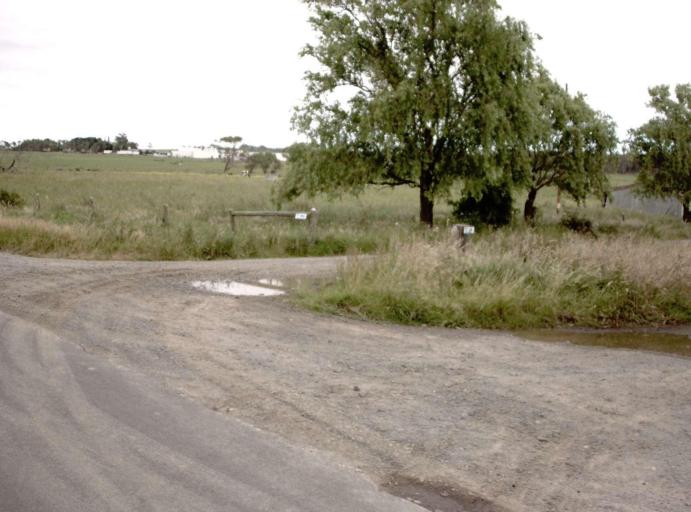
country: AU
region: Victoria
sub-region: Bass Coast
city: North Wonthaggi
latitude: -38.5509
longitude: 145.6838
